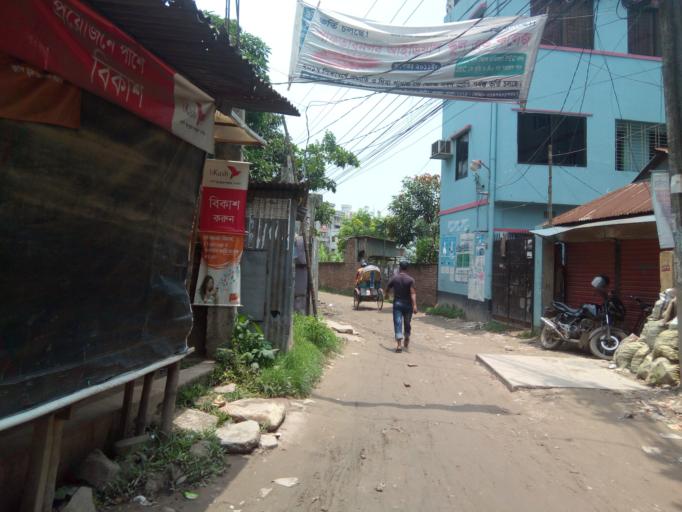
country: BD
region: Dhaka
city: Paltan
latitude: 23.7658
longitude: 90.4334
